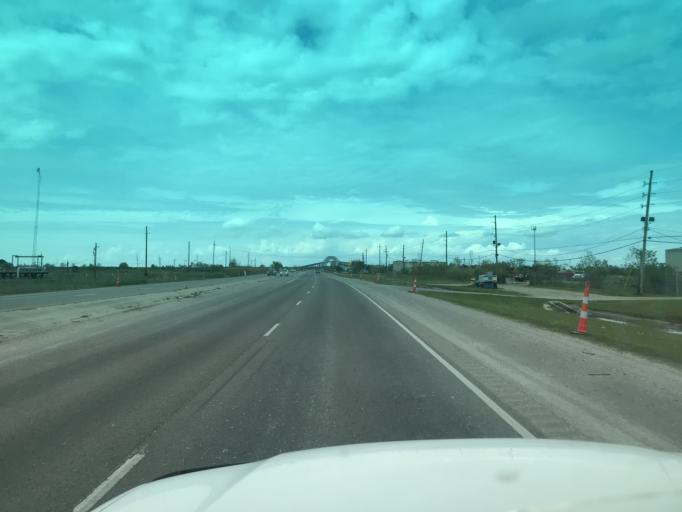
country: US
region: Louisiana
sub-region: Saint Bernard Parish
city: Chalmette
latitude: 29.9786
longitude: -89.9461
